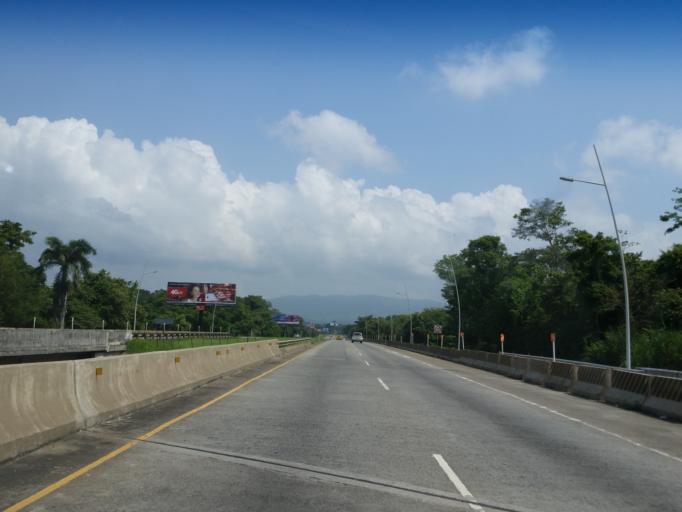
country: PA
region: Panama
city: Tocumen
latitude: 9.0560
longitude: -79.4023
